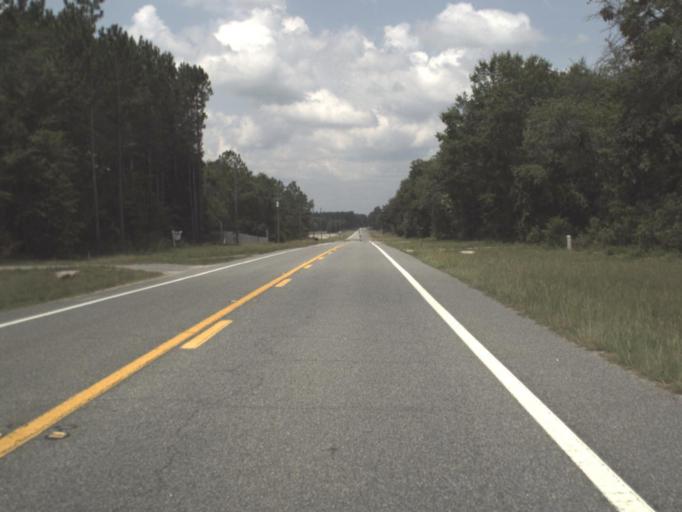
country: US
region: Florida
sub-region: Hamilton County
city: Jasper
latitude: 30.4886
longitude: -83.1702
